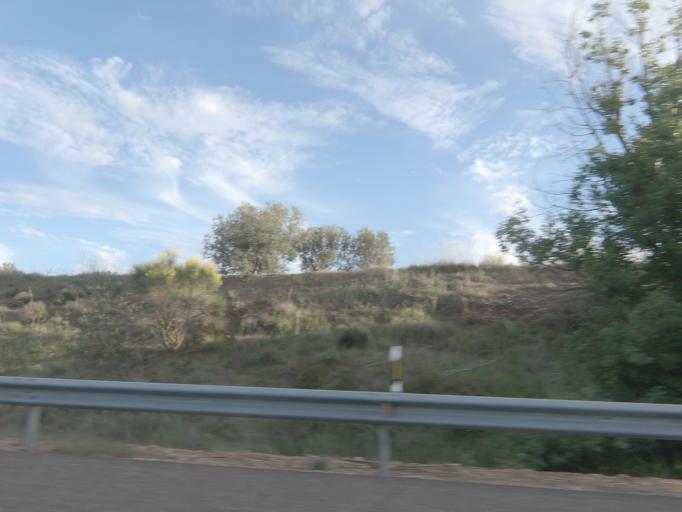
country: ES
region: Extremadura
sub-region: Provincia de Badajoz
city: Talavera La Real
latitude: 38.8628
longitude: -6.7876
